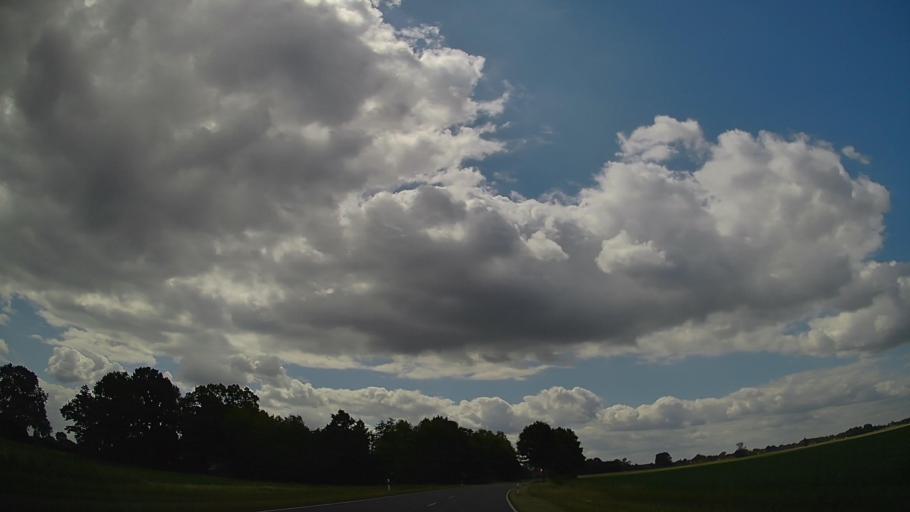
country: DE
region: Lower Saxony
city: Lembruch
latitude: 52.5443
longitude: 8.3741
